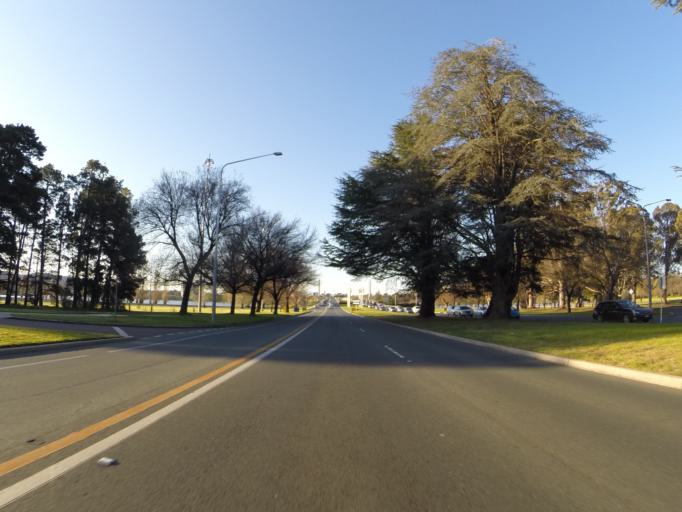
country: AU
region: Australian Capital Territory
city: Canberra
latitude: -35.2977
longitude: 149.1260
